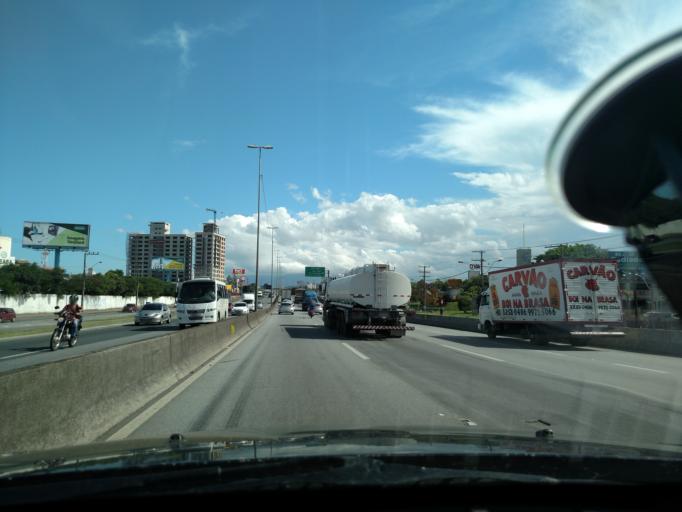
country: BR
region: Santa Catarina
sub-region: Sao Jose
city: Campinas
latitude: -27.5789
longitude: -48.6138
